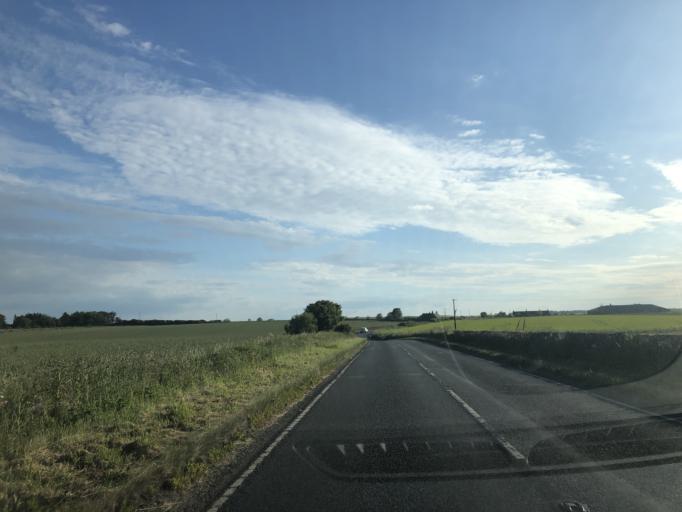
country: GB
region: Scotland
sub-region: Fife
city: Saint Monance
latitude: 56.2065
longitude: -2.7755
